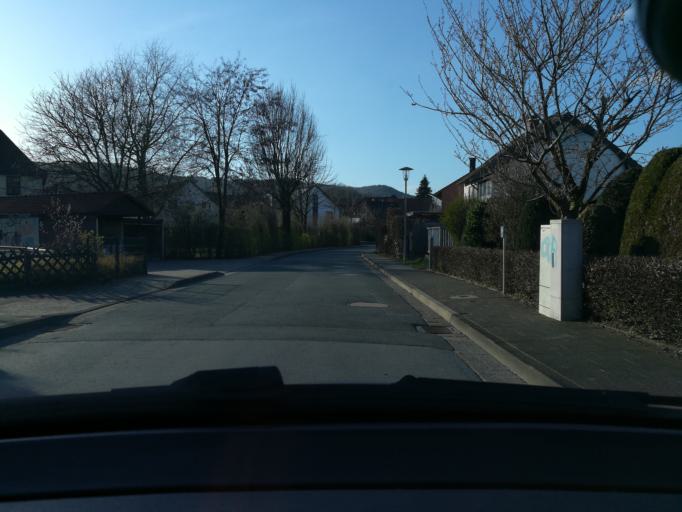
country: DE
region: North Rhine-Westphalia
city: Borgholzhausen
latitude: 52.1046
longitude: 8.3078
